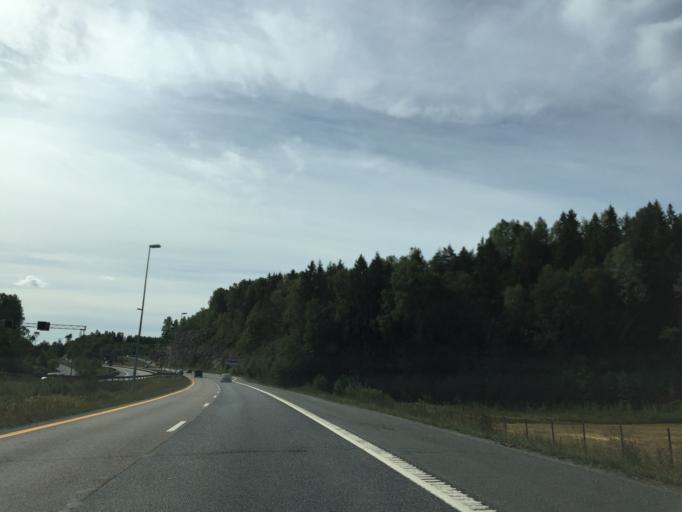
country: NO
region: Akershus
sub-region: As
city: As
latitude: 59.6944
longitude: 10.7333
